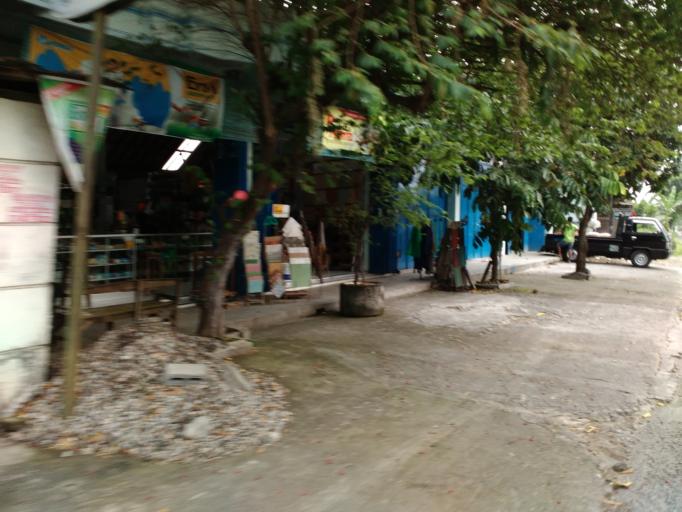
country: ID
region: Central Java
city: Delanggu
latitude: -7.5815
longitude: 110.6483
